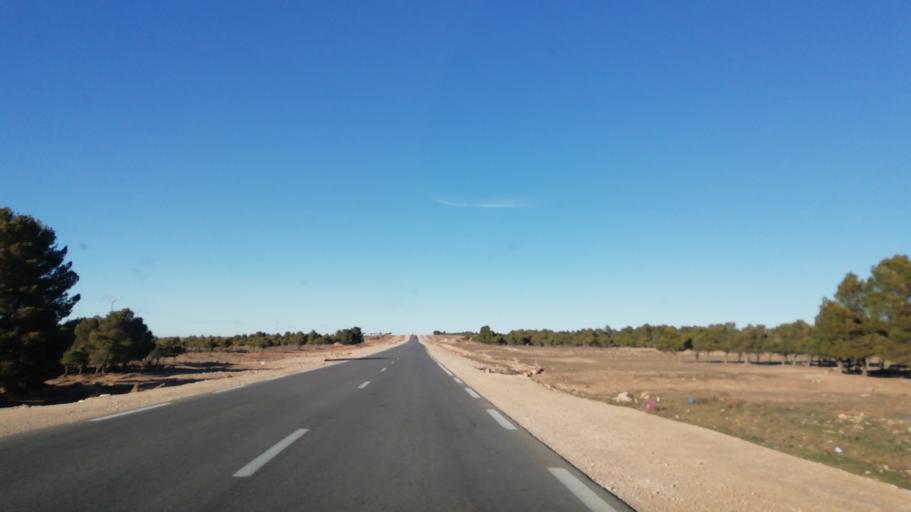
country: DZ
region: Tlemcen
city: Sebdou
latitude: 34.2517
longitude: -1.2574
